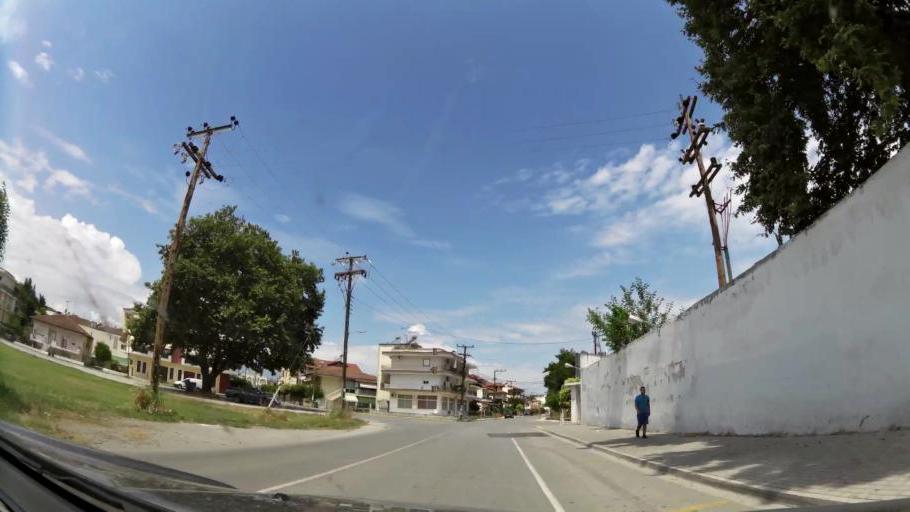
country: GR
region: Central Macedonia
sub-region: Nomos Pierias
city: Katerini
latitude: 40.2615
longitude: 22.5107
